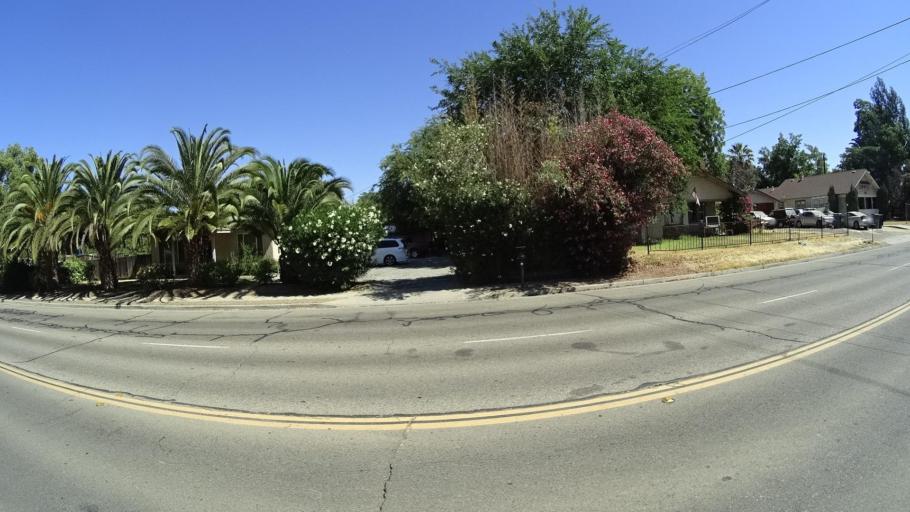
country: US
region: California
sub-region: Fresno County
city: Sunnyside
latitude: 36.7430
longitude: -119.7068
